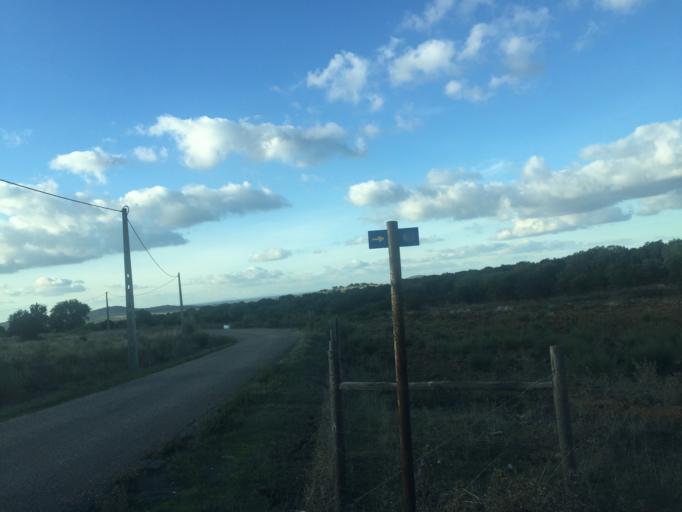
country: PT
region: Portalegre
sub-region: Alter do Chao
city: Alter do Chao
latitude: 39.1897
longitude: -7.6298
